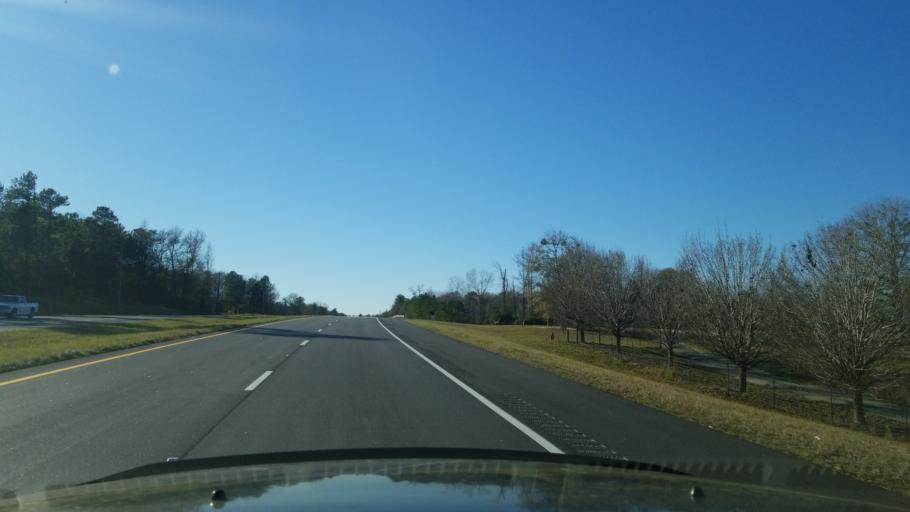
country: US
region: Georgia
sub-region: Talbot County
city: Talbotton
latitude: 32.5752
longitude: -84.5768
